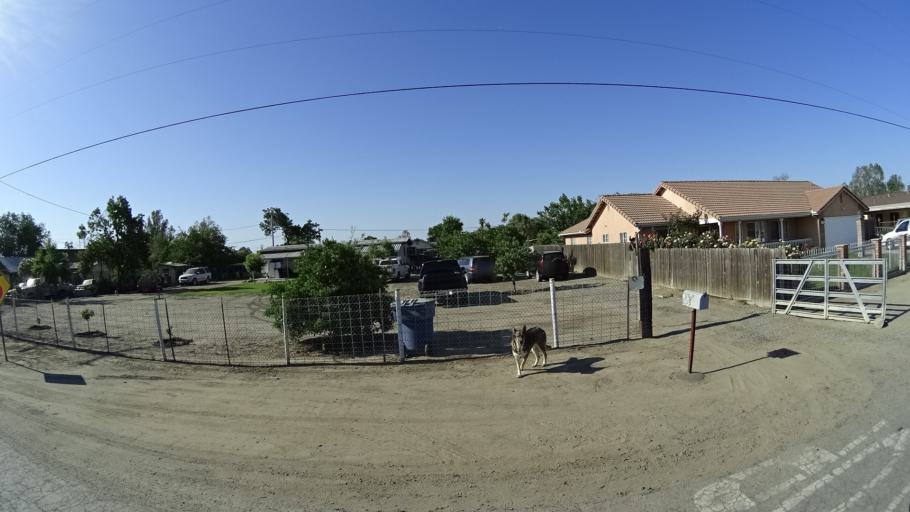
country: US
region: California
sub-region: Kings County
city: Corcoran
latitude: 36.1161
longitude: -119.5646
